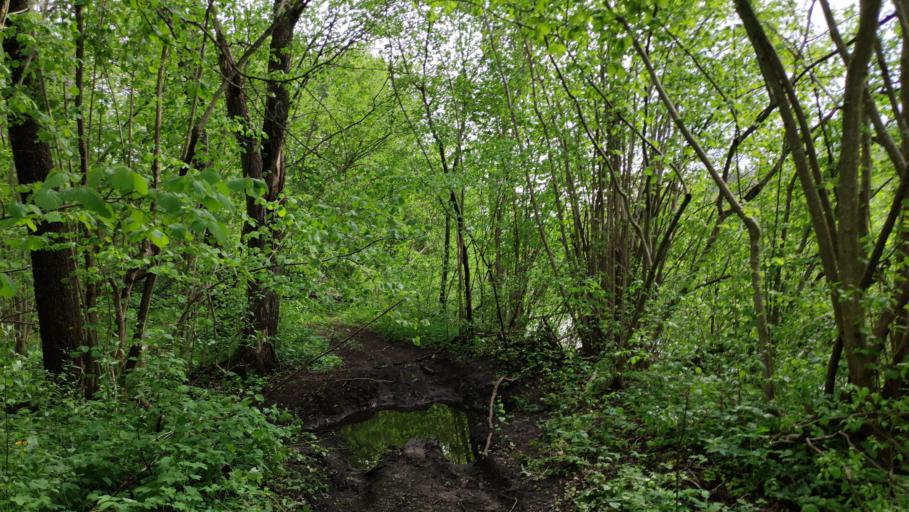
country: LT
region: Alytaus apskritis
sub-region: Alytus
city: Alytus
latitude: 54.4411
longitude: 24.0748
